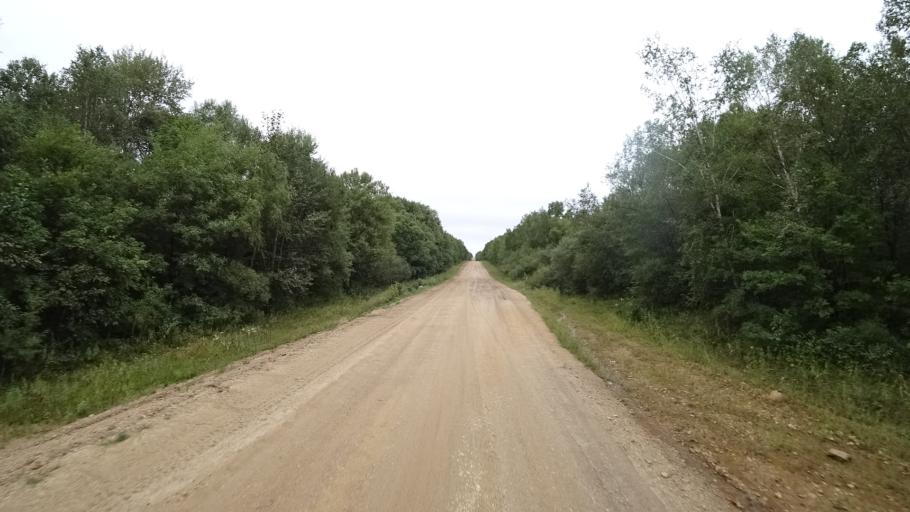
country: RU
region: Primorskiy
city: Ivanovka
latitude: 44.0371
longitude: 132.5359
